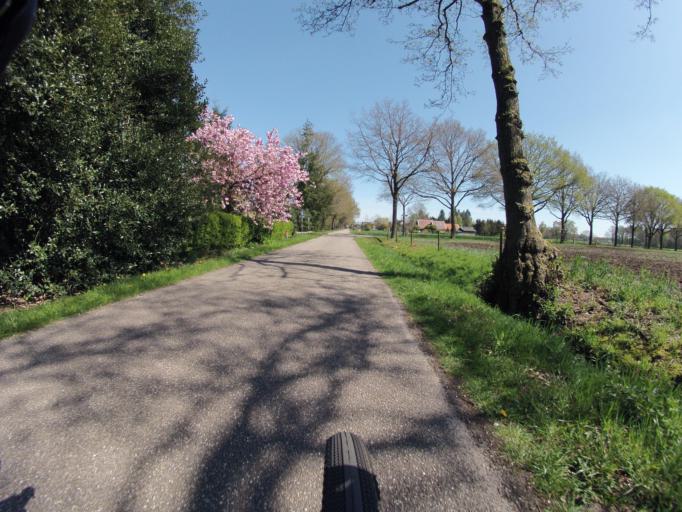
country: NL
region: Overijssel
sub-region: Gemeente Losser
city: Losser
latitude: 52.2685
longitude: 6.9745
